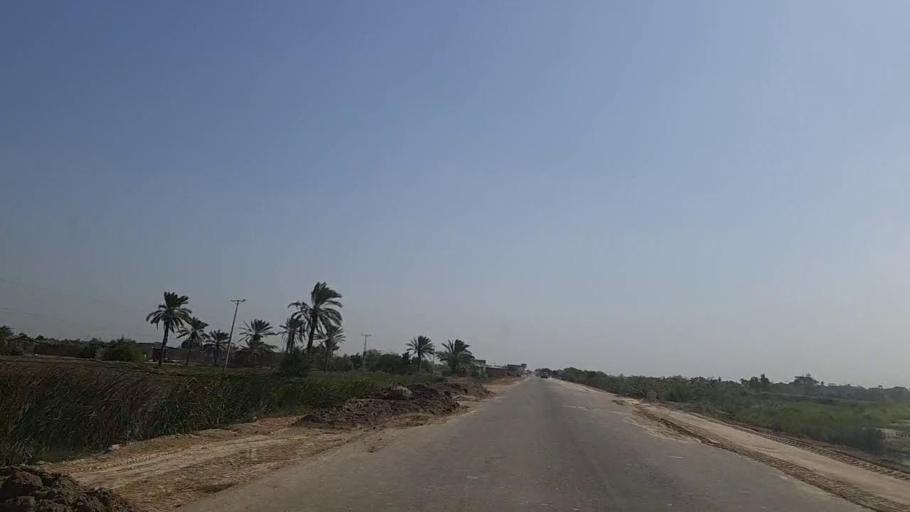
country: PK
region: Sindh
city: Daro Mehar
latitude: 24.7821
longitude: 68.1969
